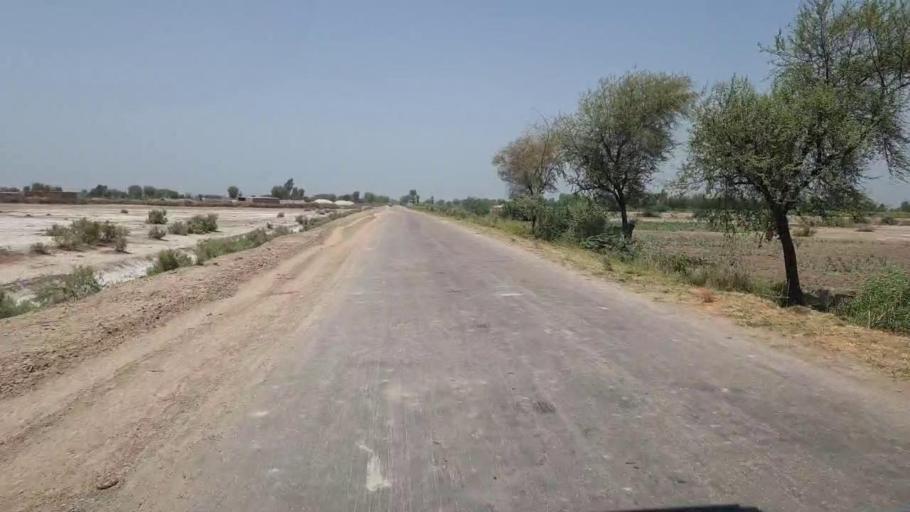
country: PK
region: Sindh
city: Nawabshah
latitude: 26.3578
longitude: 68.4017
